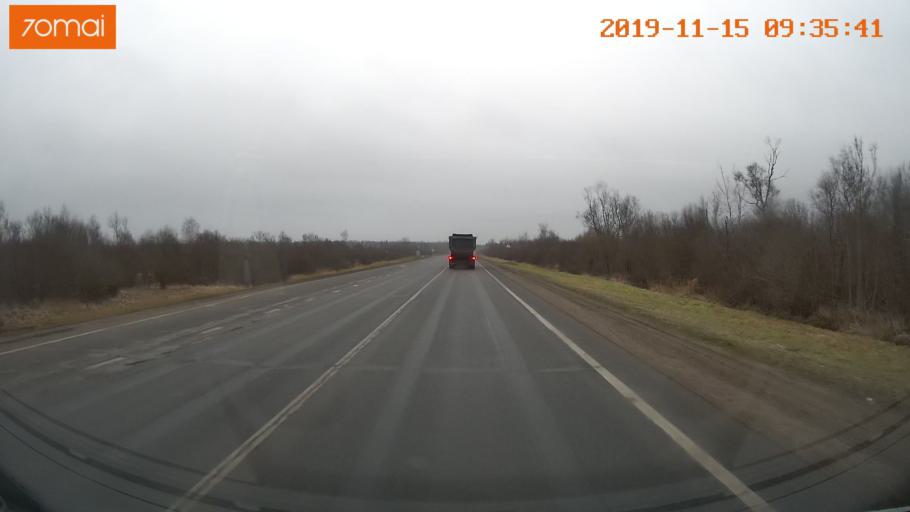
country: RU
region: Vologda
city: Sheksna
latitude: 59.2528
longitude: 38.4048
